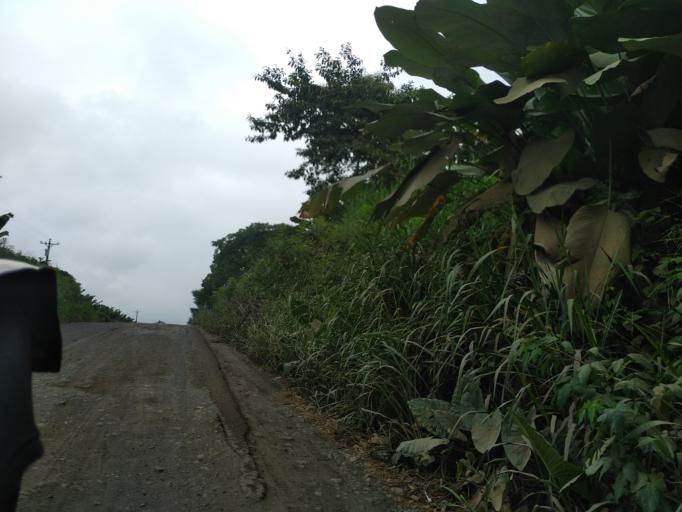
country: EC
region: Cotopaxi
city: La Mana
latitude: -0.9625
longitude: -79.3514
